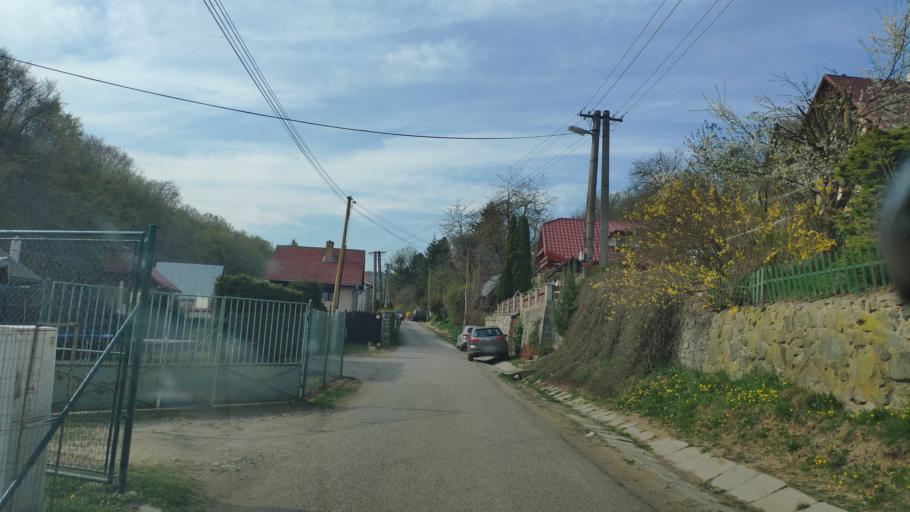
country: SK
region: Kosicky
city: Kosice
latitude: 48.7206
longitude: 21.1941
